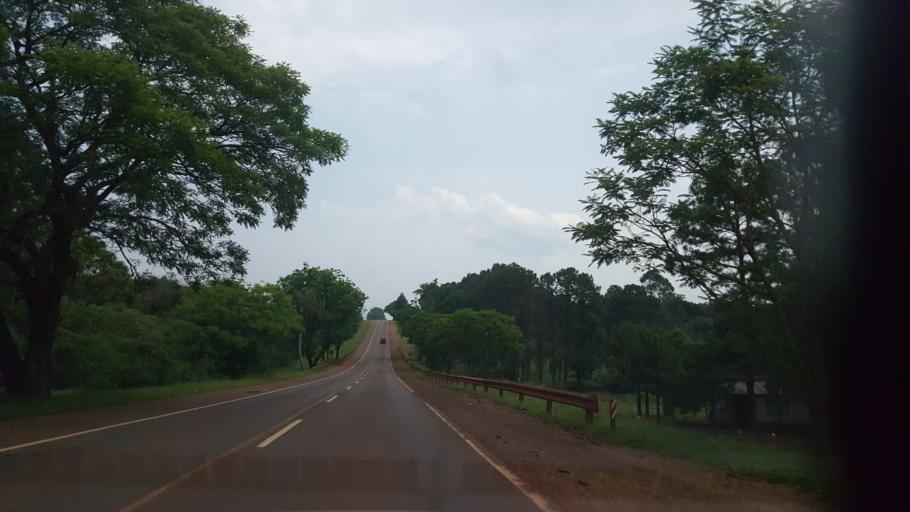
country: AR
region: Misiones
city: Jardin America
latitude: -27.0570
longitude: -55.2556
